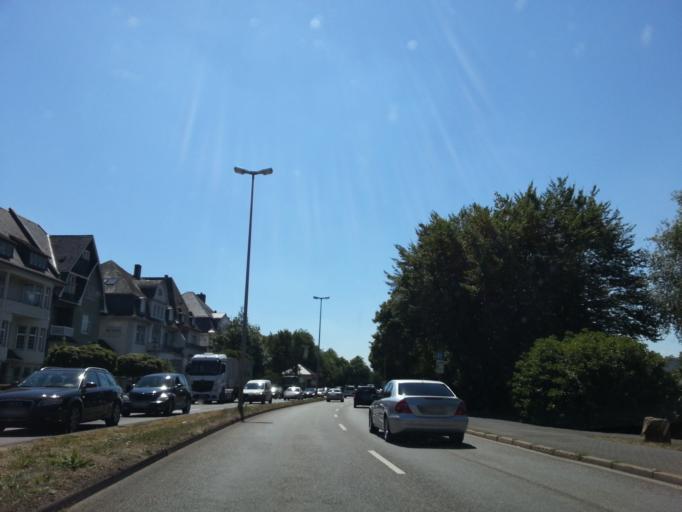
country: DE
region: Rheinland-Pfalz
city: Trier
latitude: 49.7617
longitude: 6.6330
